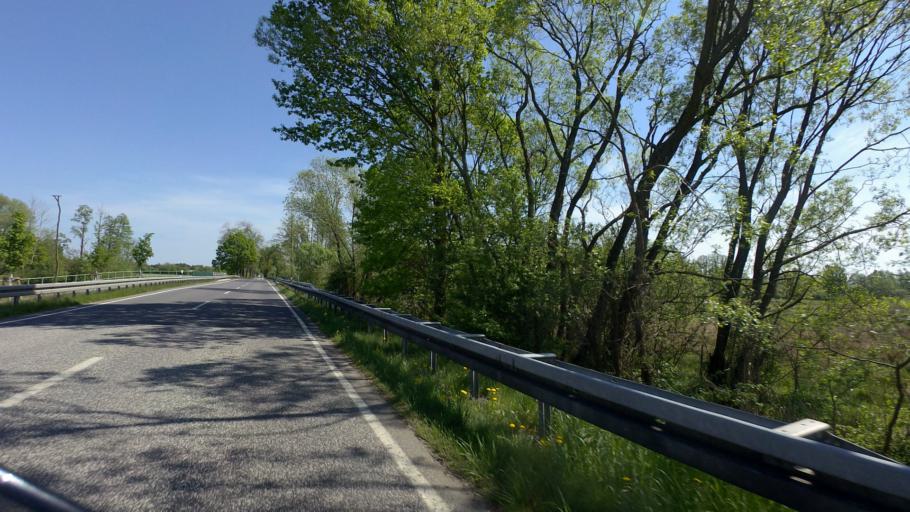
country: DE
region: Brandenburg
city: Schlepzig
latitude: 52.0786
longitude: 13.8830
